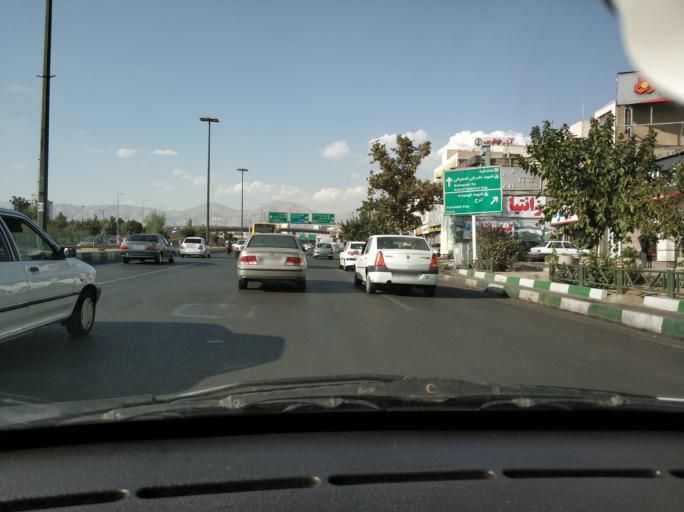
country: IR
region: Tehran
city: Tehran
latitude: 35.7080
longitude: 51.3371
